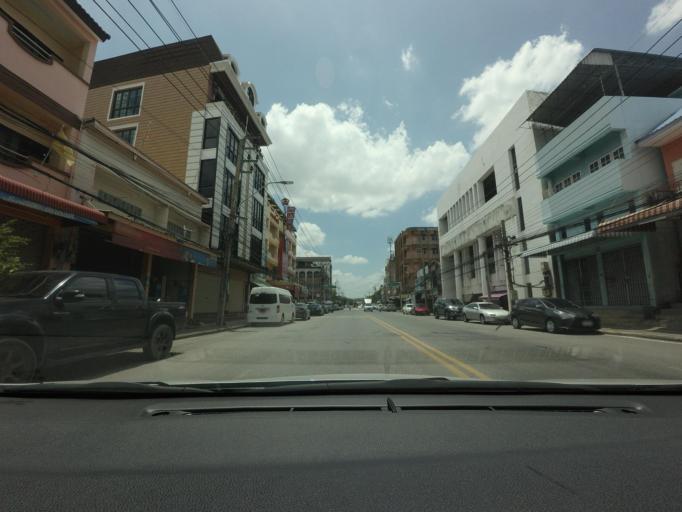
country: TH
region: Samut Prakan
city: Samut Prakan
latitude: 13.5862
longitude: 100.5957
